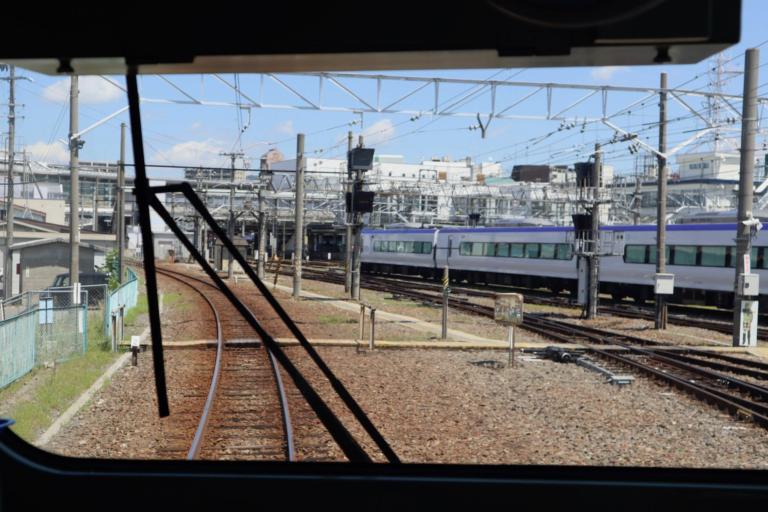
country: JP
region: Nagano
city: Matsumoto
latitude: 36.2292
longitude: 137.9643
